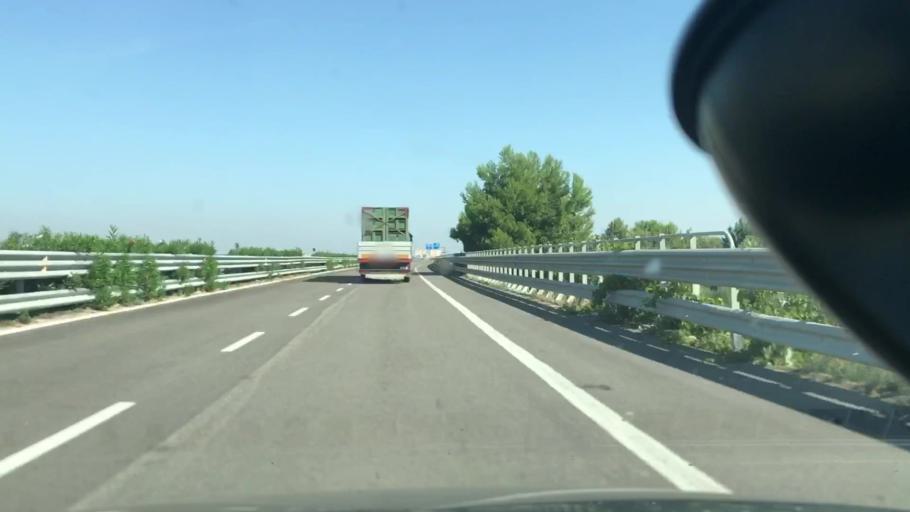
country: IT
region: Apulia
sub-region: Provincia di Foggia
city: Foggia
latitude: 41.4188
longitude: 15.5588
